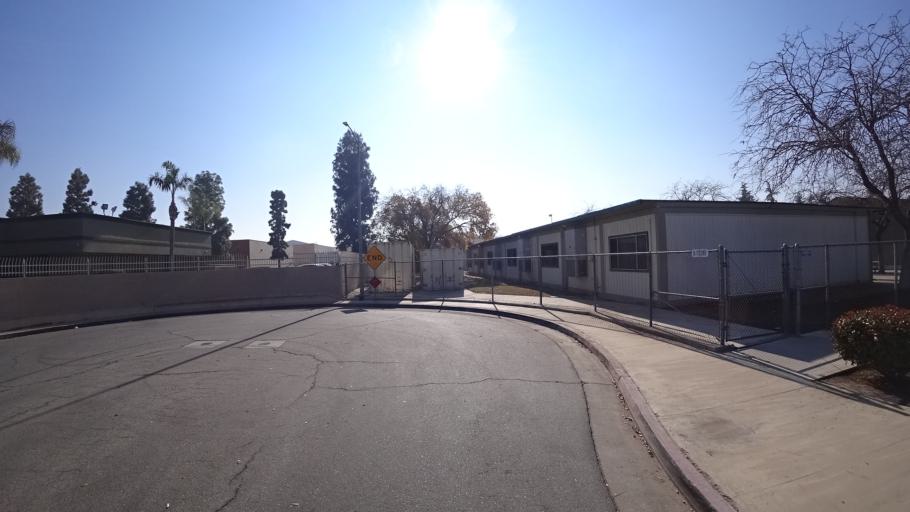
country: US
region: California
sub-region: Kern County
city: Bakersfield
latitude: 35.3565
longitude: -119.0632
